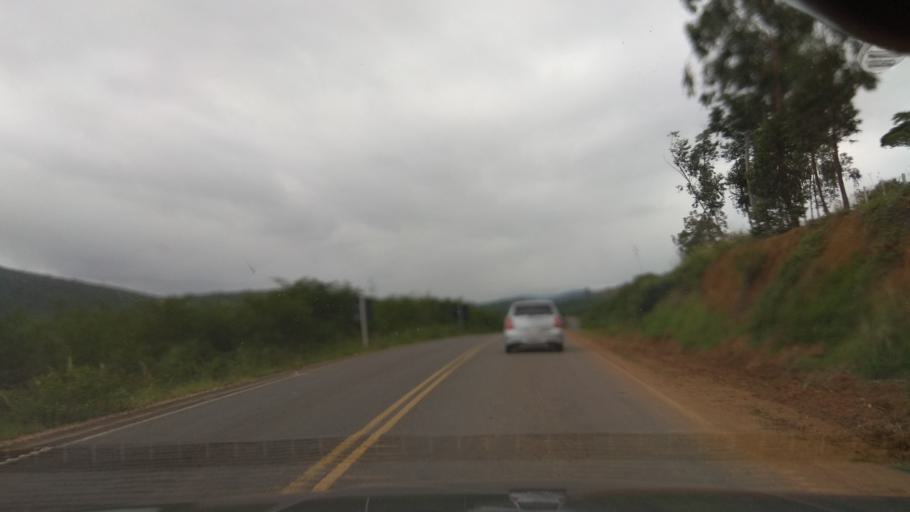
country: BR
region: Bahia
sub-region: Santa Ines
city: Santa Ines
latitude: -13.2725
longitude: -39.8055
